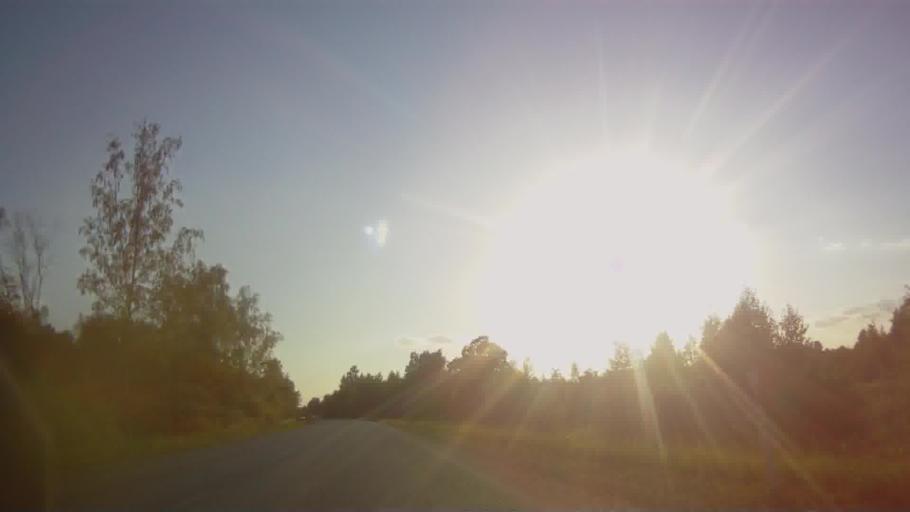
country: LV
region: Livani
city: Livani
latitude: 56.5290
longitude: 26.3900
